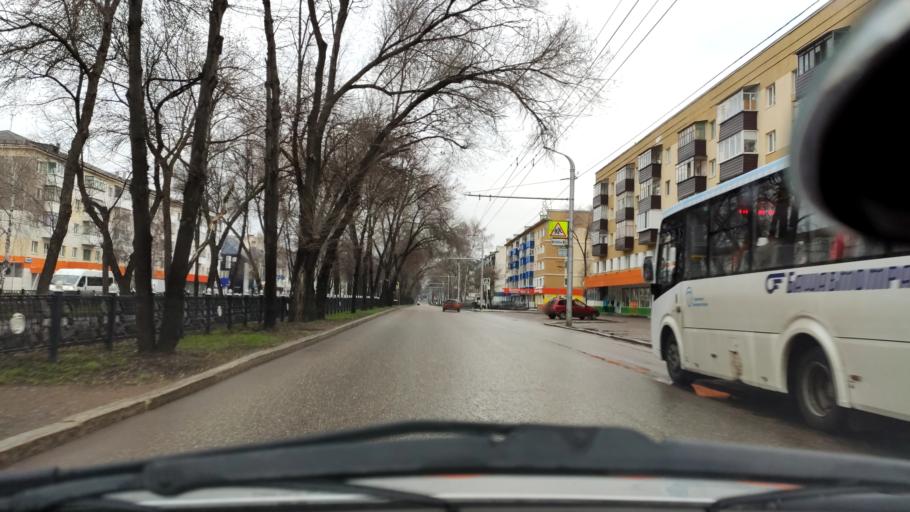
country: RU
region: Bashkortostan
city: Sterlitamak
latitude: 53.6390
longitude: 55.9384
